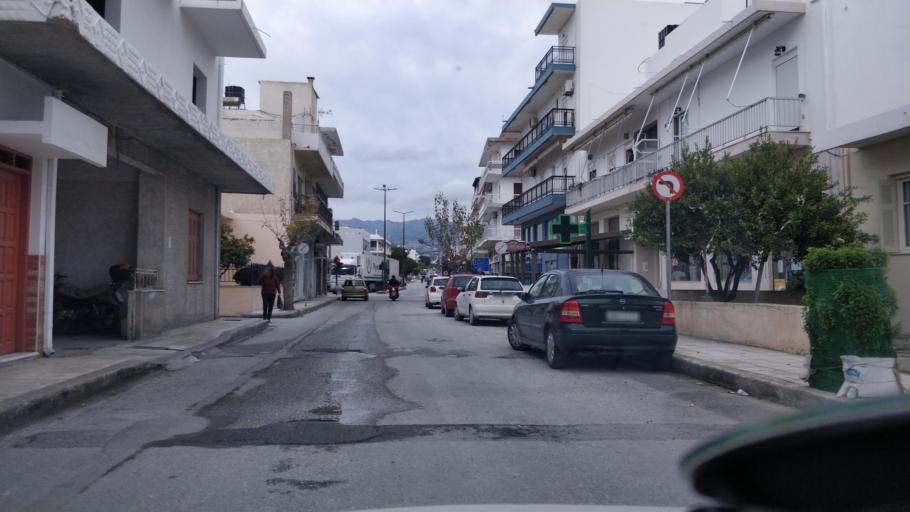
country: GR
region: Crete
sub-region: Nomos Lasithiou
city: Ierapetra
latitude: 35.0080
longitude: 25.7353
